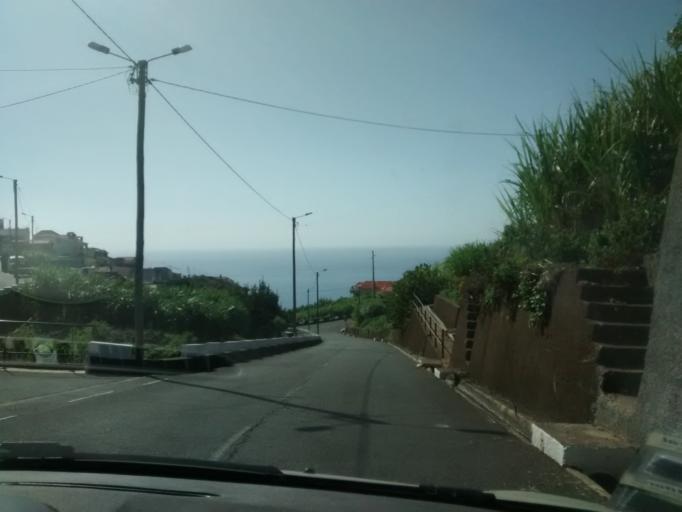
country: PT
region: Madeira
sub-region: Calheta
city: Arco da Calheta
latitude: 32.7250
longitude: -17.1660
